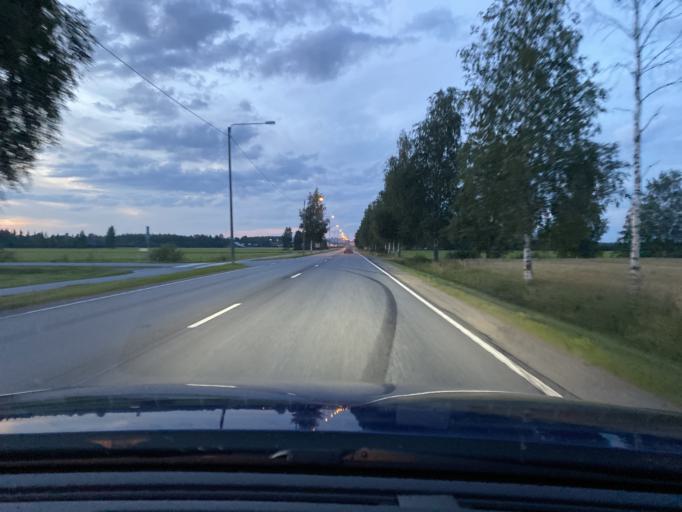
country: FI
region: Southern Ostrobothnia
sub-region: Suupohja
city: Kauhajoki
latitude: 62.4373
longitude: 22.2076
